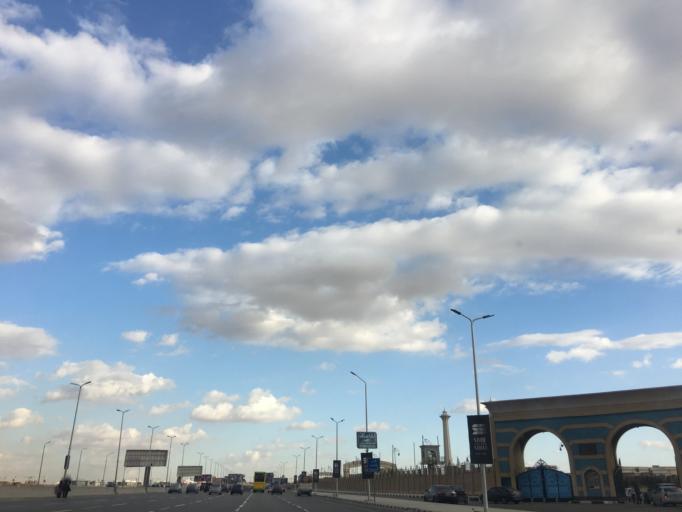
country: EG
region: Muhafazat al Qahirah
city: Cairo
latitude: 30.0203
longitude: 31.3782
